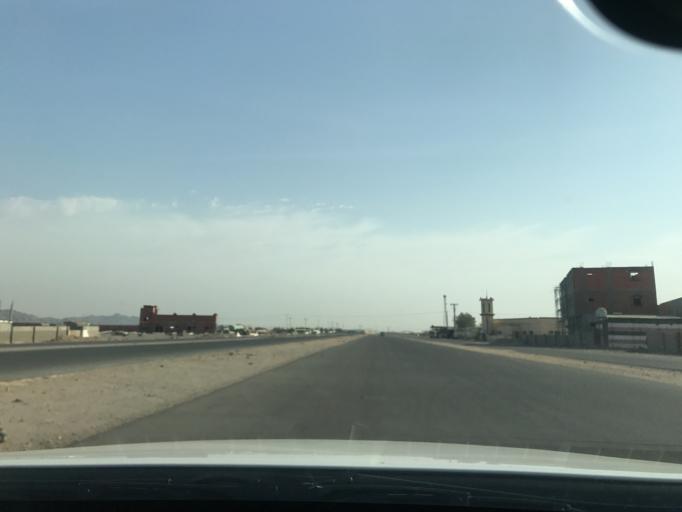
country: SA
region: Makkah
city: Al Jumum
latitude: 21.4493
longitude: 39.5212
